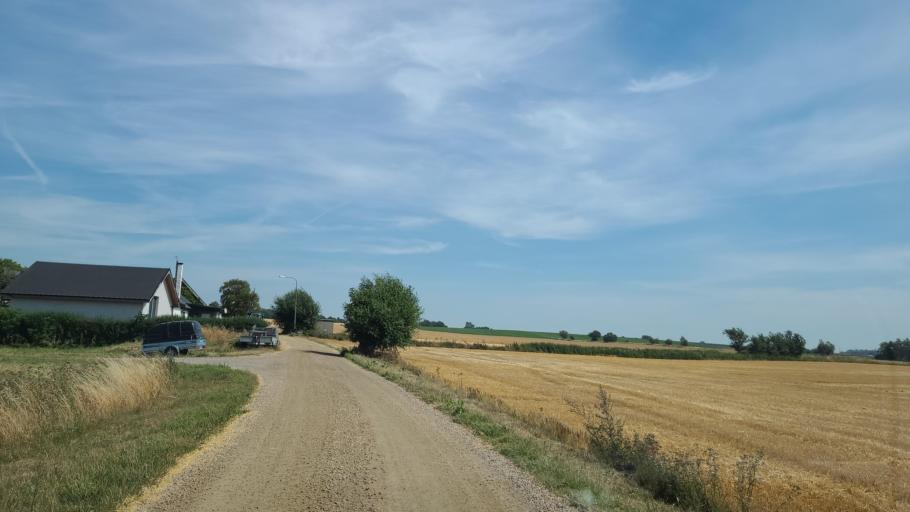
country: SE
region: Skane
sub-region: Trelleborgs Kommun
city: Skare
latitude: 55.4238
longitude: 13.0647
